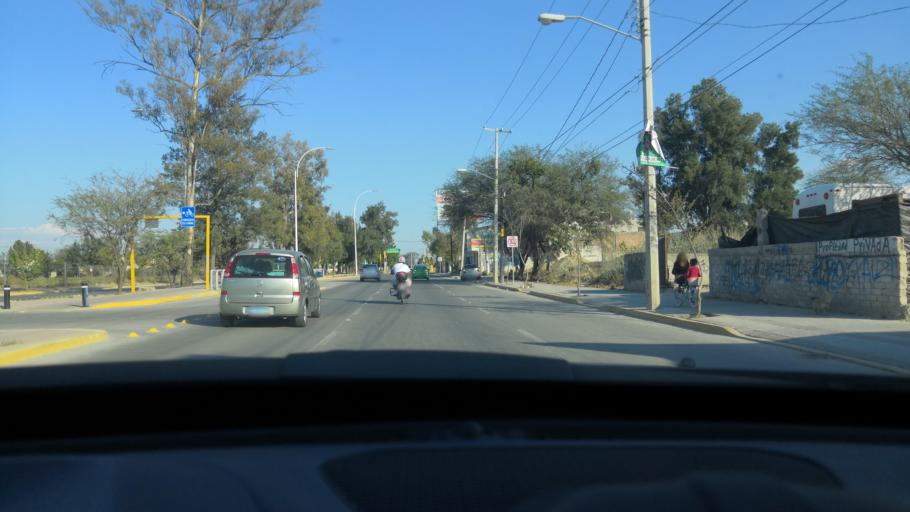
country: MX
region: Guanajuato
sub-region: Leon
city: San Jose de Duran (Los Troncoso)
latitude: 21.0605
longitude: -101.6141
